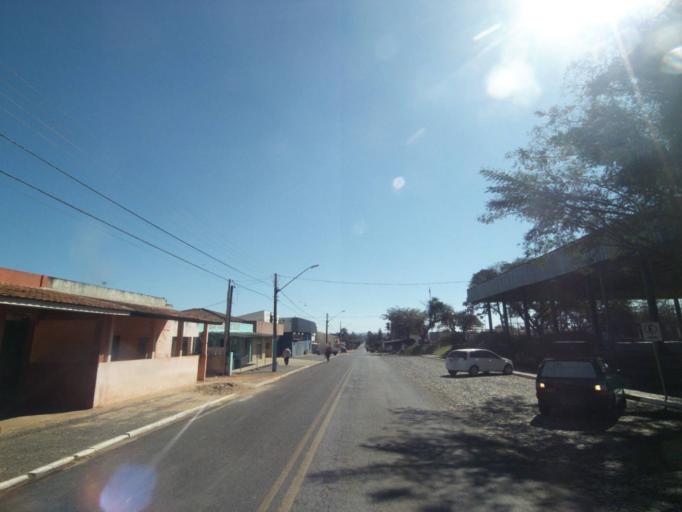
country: BR
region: Parana
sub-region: Tibagi
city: Tibagi
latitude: -24.5215
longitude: -50.4061
